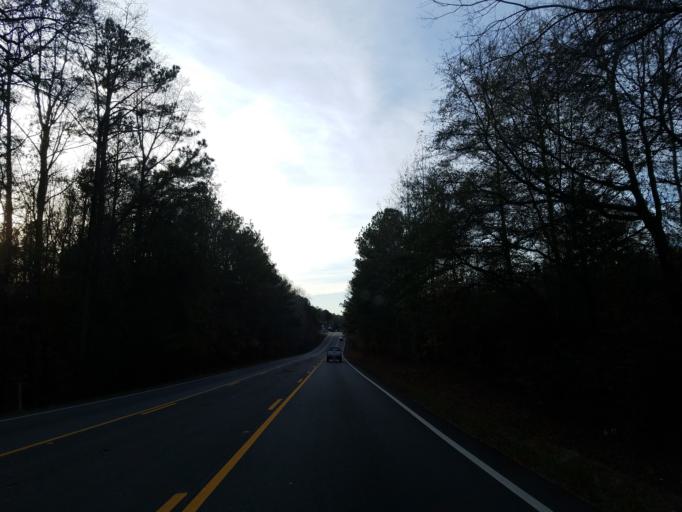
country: US
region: Georgia
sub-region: Carroll County
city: Temple
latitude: 33.7312
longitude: -85.0312
